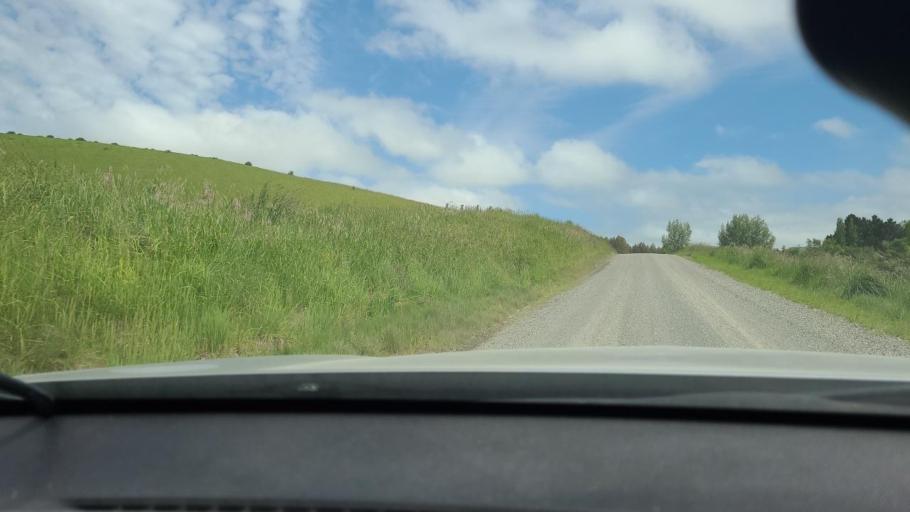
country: NZ
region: Southland
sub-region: Southland District
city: Riverton
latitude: -45.9087
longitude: 167.9494
